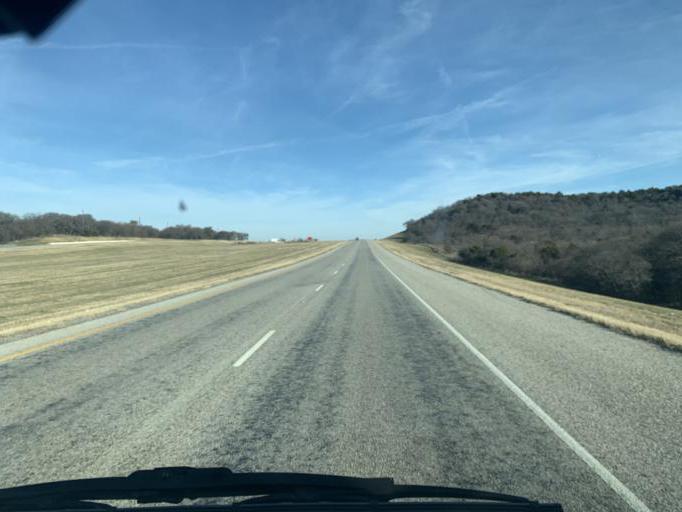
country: US
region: Texas
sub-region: Dallas County
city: Cedar Hill
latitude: 32.6263
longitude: -96.9754
